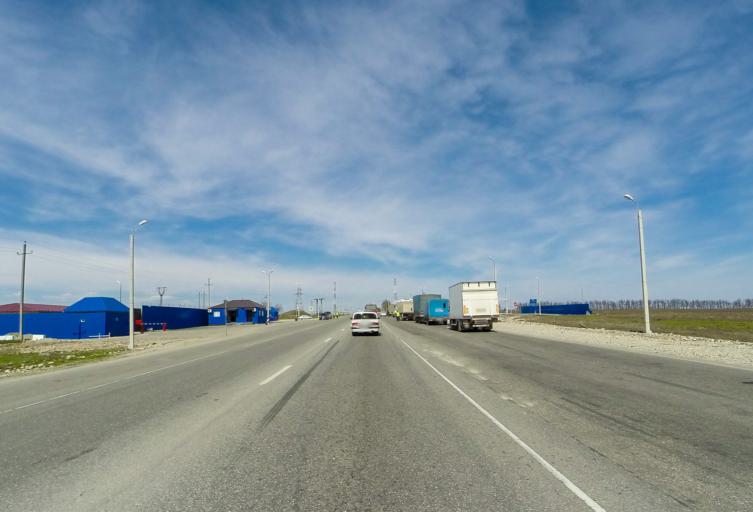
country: RU
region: Kabardino-Balkariya
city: Malka
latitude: 43.8055
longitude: 43.3675
